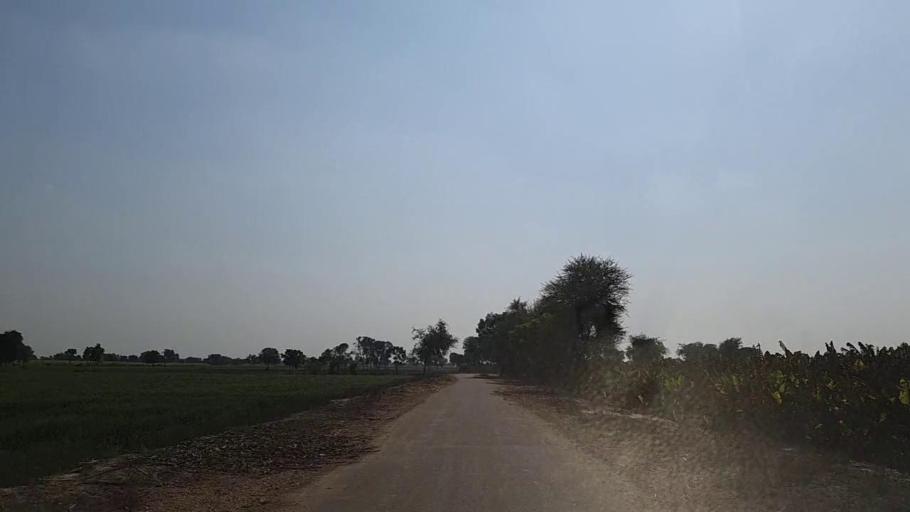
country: PK
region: Sindh
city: Daur
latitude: 26.4896
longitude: 68.2518
